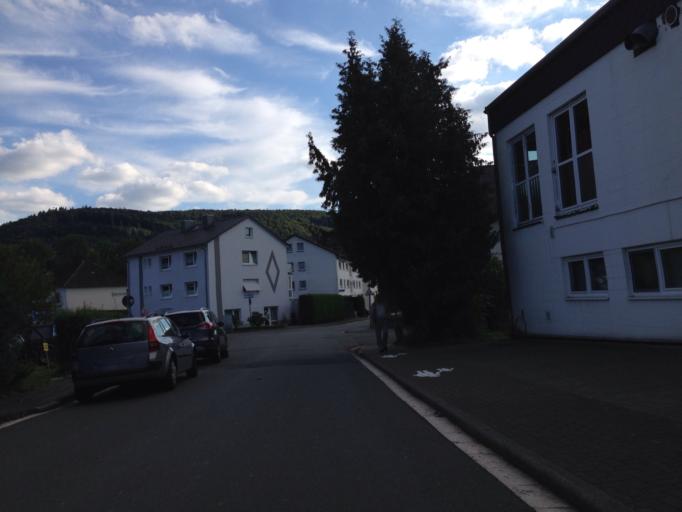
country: DE
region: Hesse
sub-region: Regierungsbezirk Giessen
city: Biedenkopf
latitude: 50.9165
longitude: 8.5189
